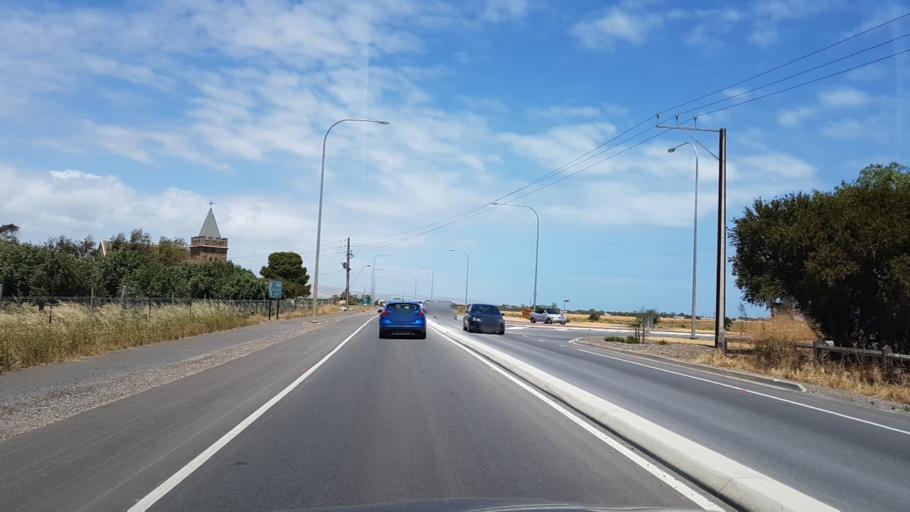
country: AU
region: South Australia
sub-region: Onkaparinga
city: Aldinga
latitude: -35.2692
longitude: 138.4840
